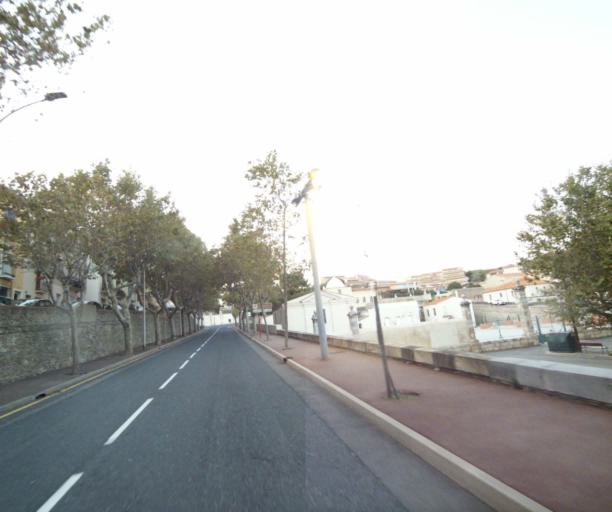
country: FR
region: Languedoc-Roussillon
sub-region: Departement des Pyrenees-Orientales
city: Portvendres
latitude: 42.5204
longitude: 3.1065
